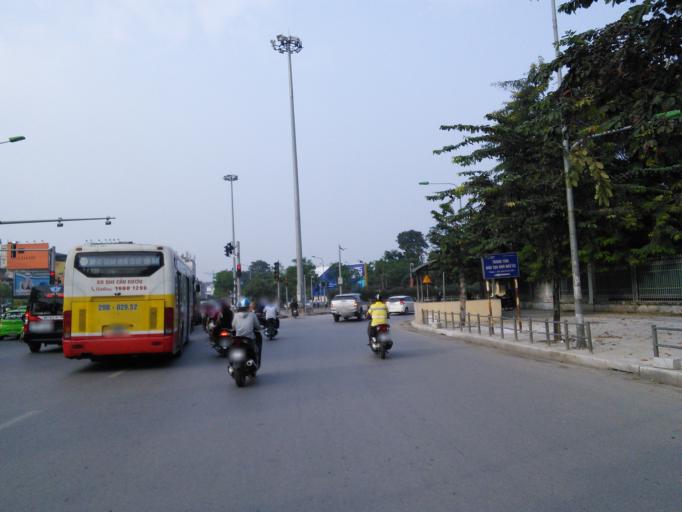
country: VN
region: Ha Noi
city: Hai BaTrung
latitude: 21.0071
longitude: 105.8415
